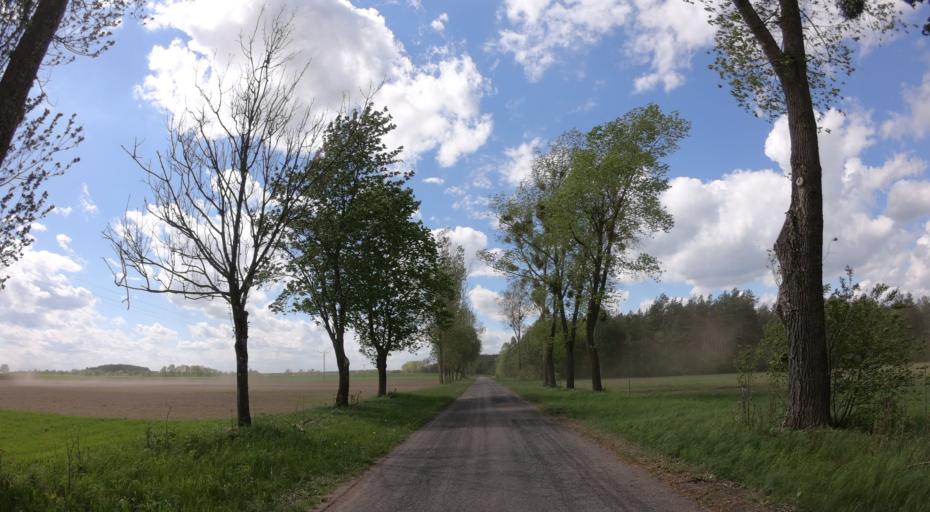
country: PL
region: West Pomeranian Voivodeship
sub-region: Powiat lobeski
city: Lobez
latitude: 53.6035
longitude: 15.6784
